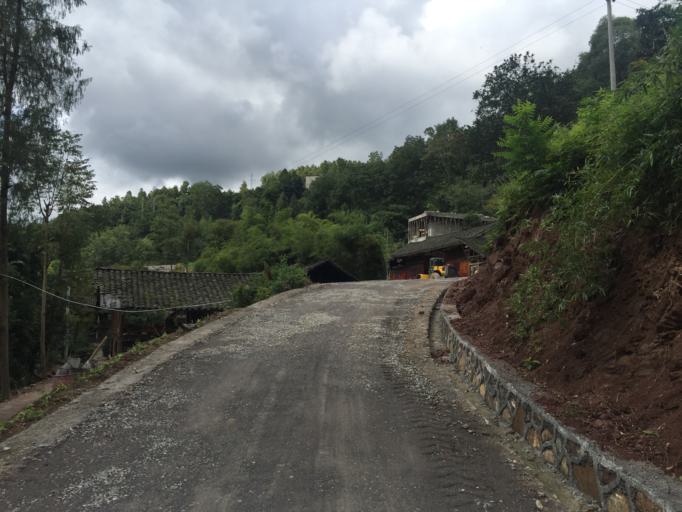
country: CN
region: Guizhou Sheng
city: Xujiaba
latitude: 27.6845
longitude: 108.0844
